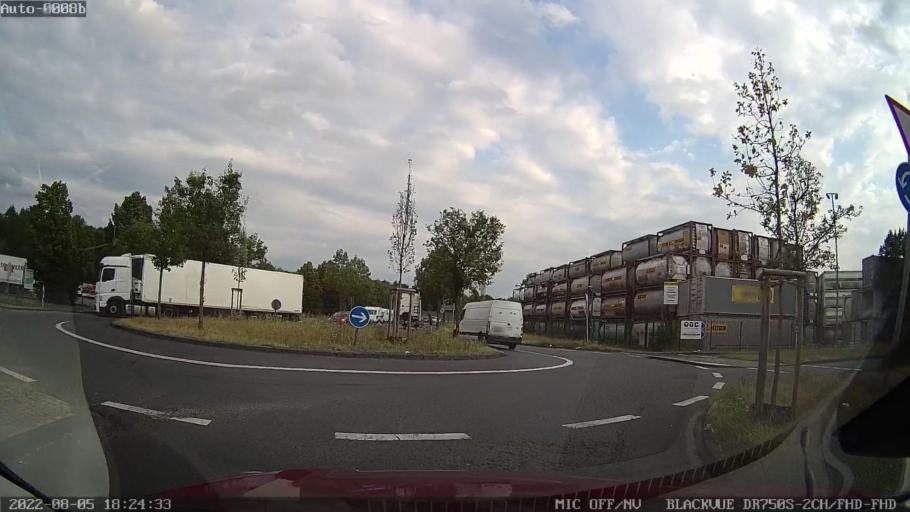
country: DE
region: North Rhine-Westphalia
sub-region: Regierungsbezirk Koln
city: Neustadt/Sued
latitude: 50.8877
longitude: 6.9241
